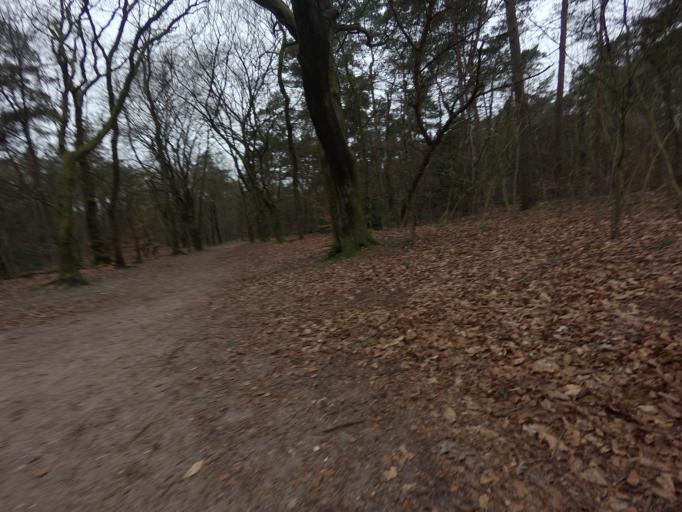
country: NL
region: Utrecht
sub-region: Gemeente Utrechtse Heuvelrug
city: Doorn
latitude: 52.0429
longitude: 5.3520
